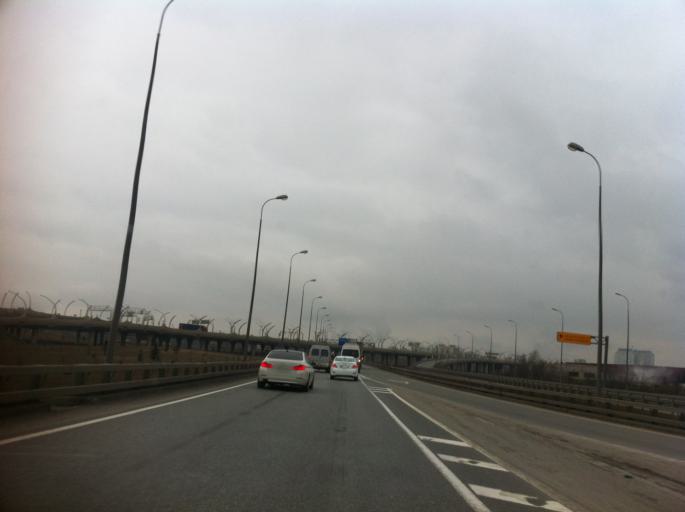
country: RU
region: St.-Petersburg
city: Dachnoye
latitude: 59.8330
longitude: 30.2843
